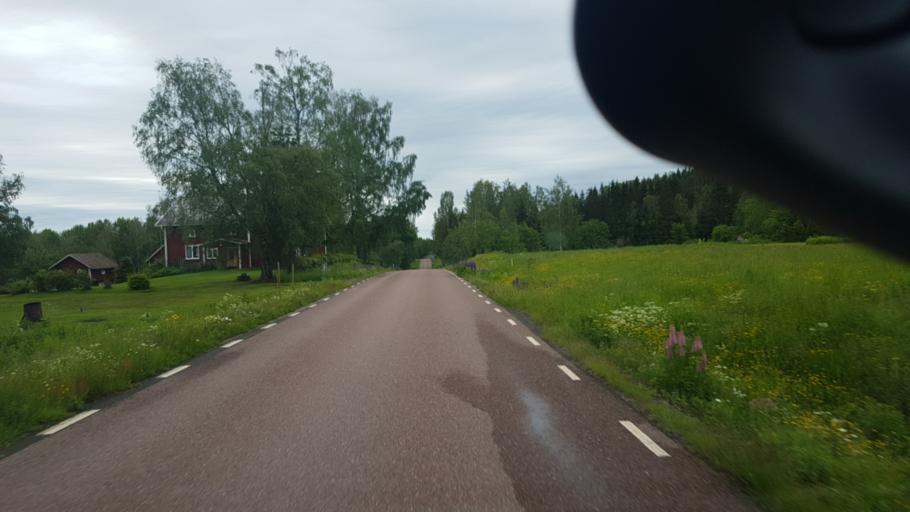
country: NO
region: Ostfold
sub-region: Romskog
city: Romskog
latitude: 59.7331
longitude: 12.0622
